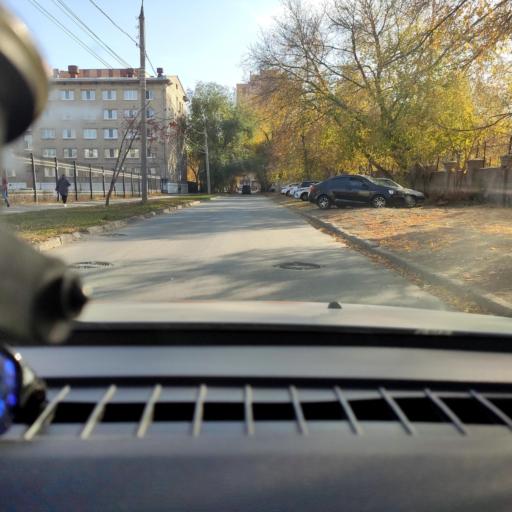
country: RU
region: Samara
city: Samara
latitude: 53.2018
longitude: 50.1665
